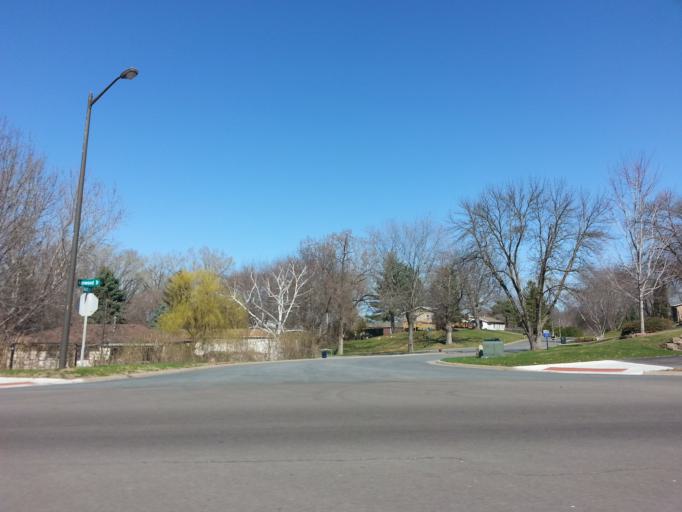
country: US
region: Minnesota
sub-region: Dakota County
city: Burnsville
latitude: 44.7090
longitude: -93.2937
